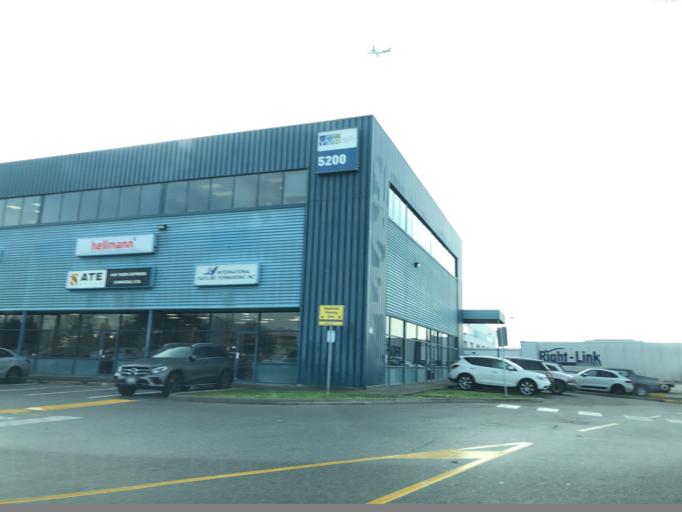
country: CA
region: British Columbia
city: Richmond
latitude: 49.1921
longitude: -123.1672
